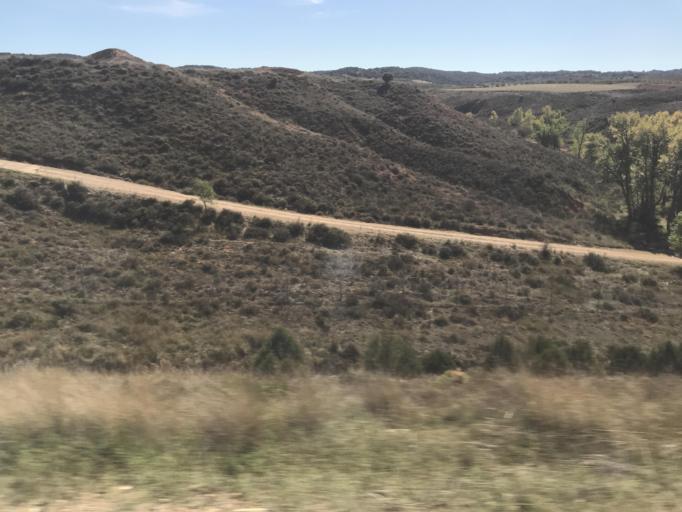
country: ES
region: Aragon
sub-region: Provincia de Zaragoza
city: Contamina
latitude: 41.2771
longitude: -1.9184
